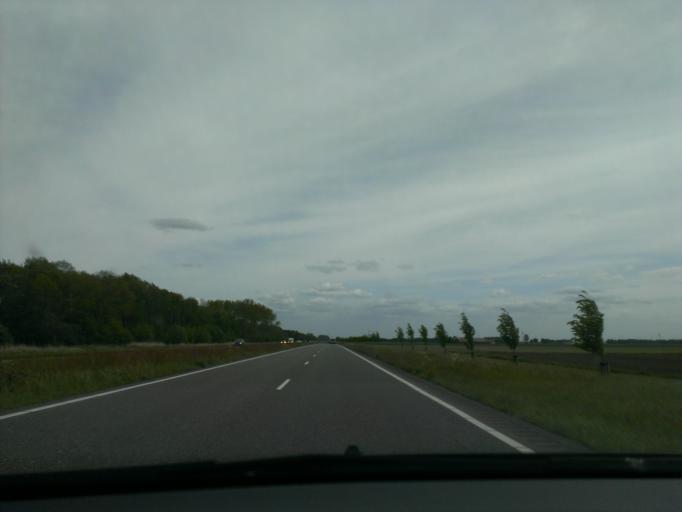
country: NL
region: Flevoland
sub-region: Gemeente Lelystad
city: Lelystad
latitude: 52.4532
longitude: 5.5416
